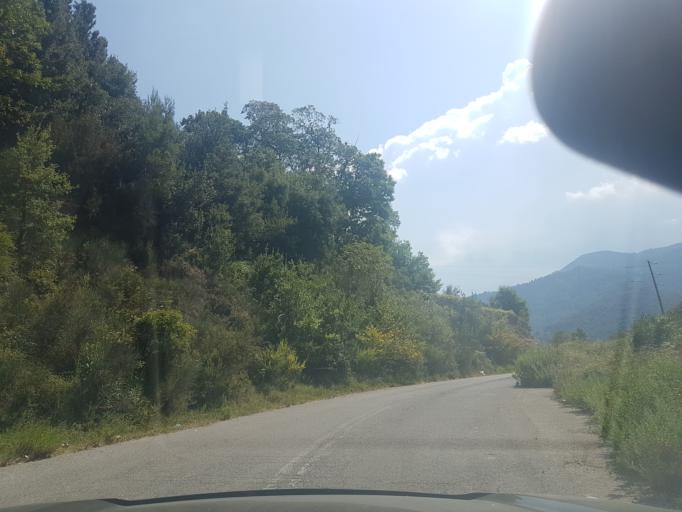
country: GR
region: Central Greece
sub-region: Nomos Evvoias
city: Yimnon
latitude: 38.6253
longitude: 23.8909
